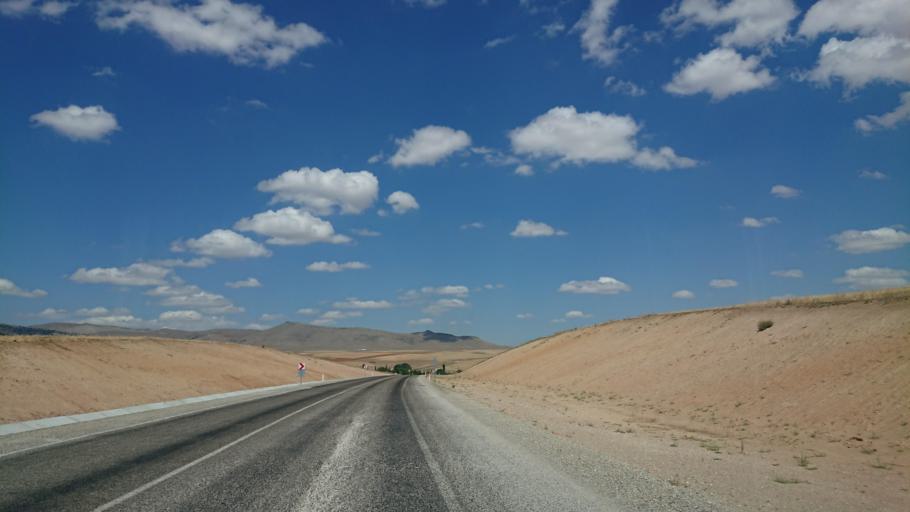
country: TR
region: Ankara
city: Evren
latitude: 39.1209
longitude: 33.9523
